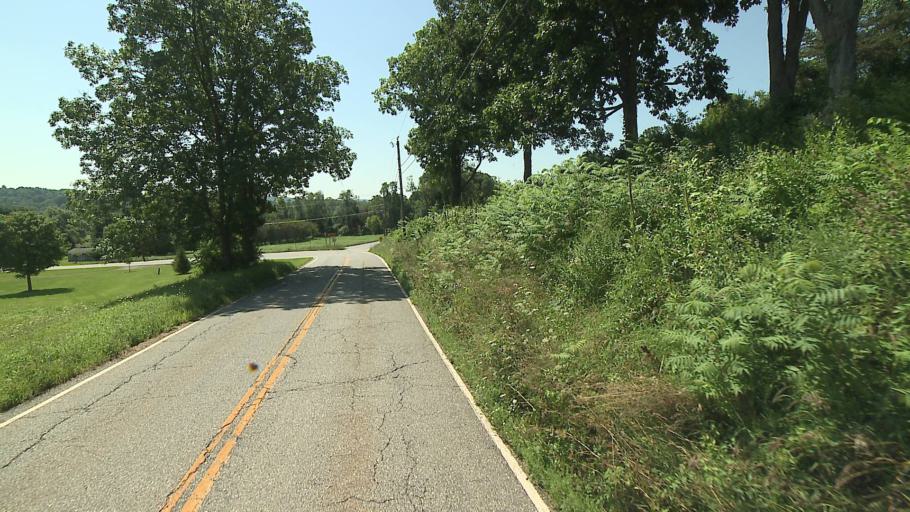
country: US
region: Connecticut
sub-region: Litchfield County
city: Kent
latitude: 41.8947
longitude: -73.4880
